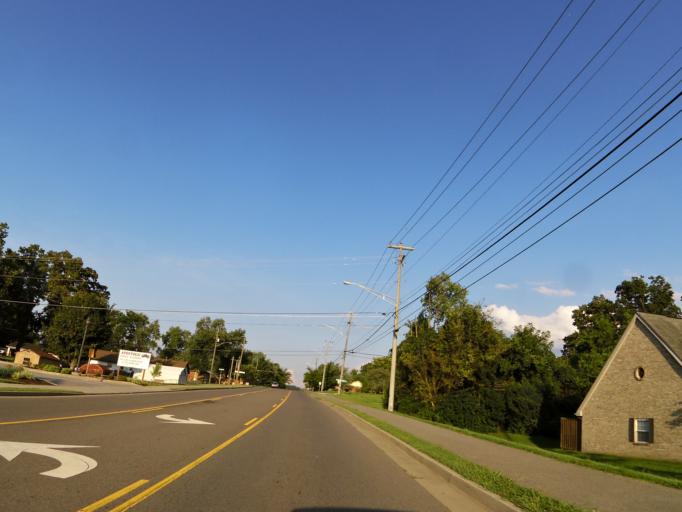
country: US
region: Tennessee
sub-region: Knox County
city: Knoxville
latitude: 35.9867
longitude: -83.9926
